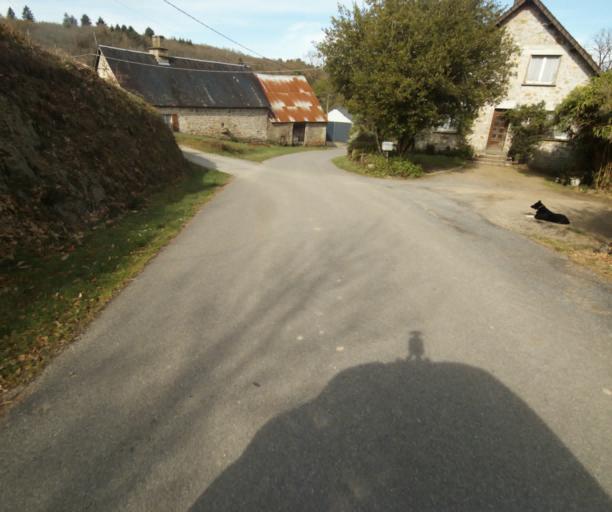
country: FR
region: Limousin
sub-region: Departement de la Correze
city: Correze
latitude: 45.3417
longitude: 1.8556
